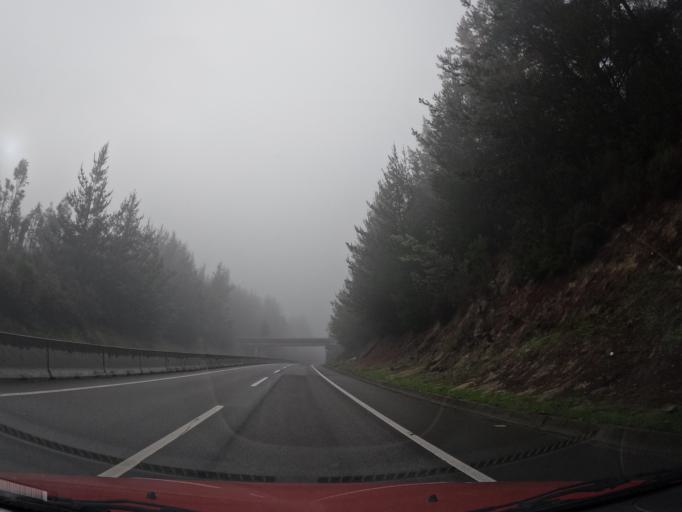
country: CL
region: Biobio
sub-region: Provincia de Concepcion
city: Tome
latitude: -36.7324
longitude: -72.8037
